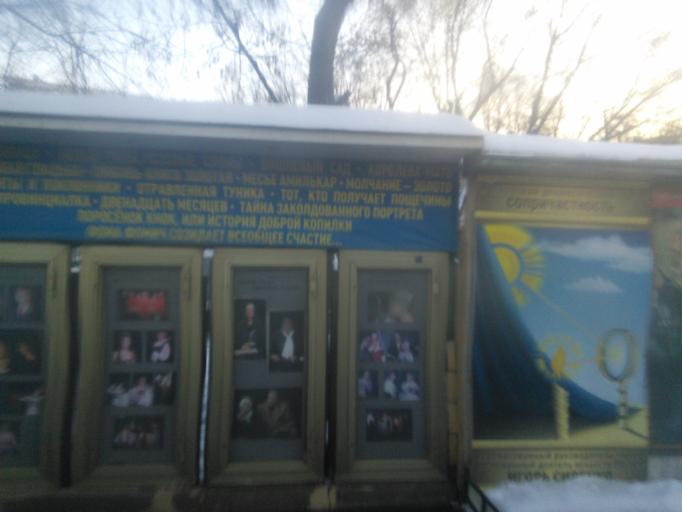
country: RU
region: Moscow
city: Lefortovo
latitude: 55.7639
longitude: 37.6728
